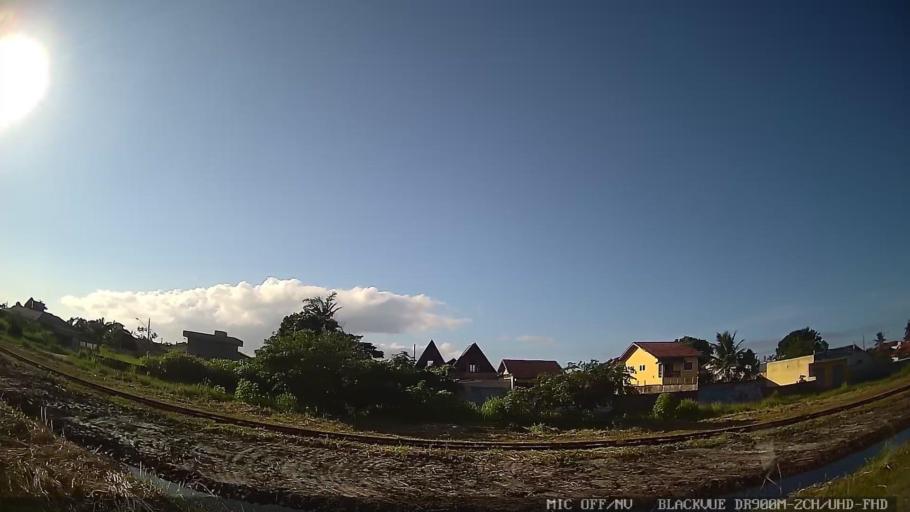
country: BR
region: Sao Paulo
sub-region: Peruibe
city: Peruibe
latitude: -24.2774
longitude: -46.9555
